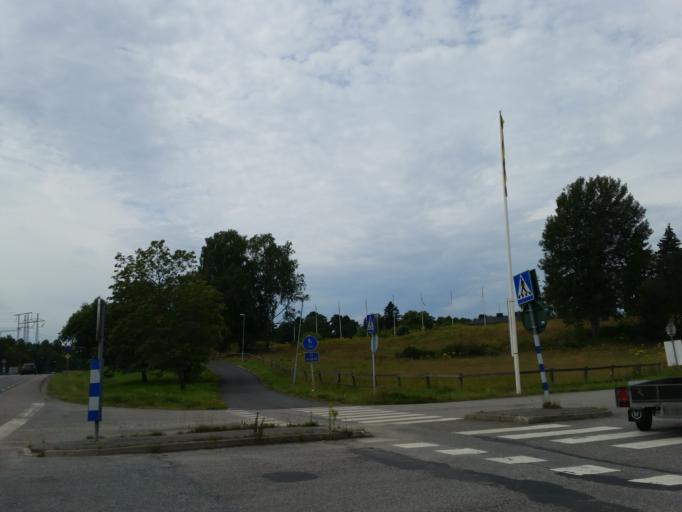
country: SE
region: Stockholm
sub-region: Botkyrka Kommun
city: Alby
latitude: 59.2220
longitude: 17.8349
